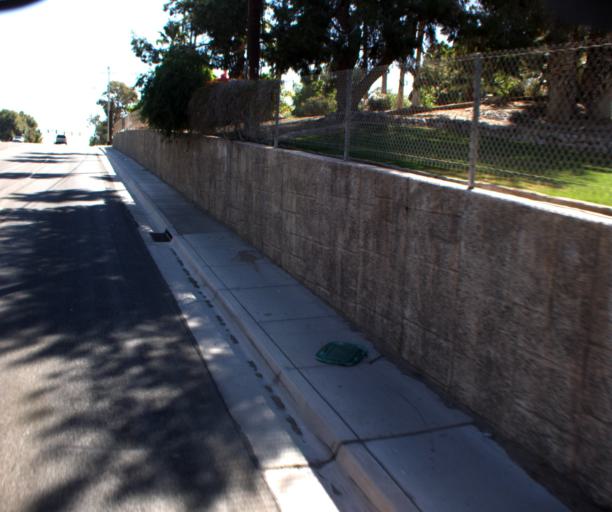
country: US
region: Arizona
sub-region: Yuma County
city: Yuma
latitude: 32.6984
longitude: -114.6402
